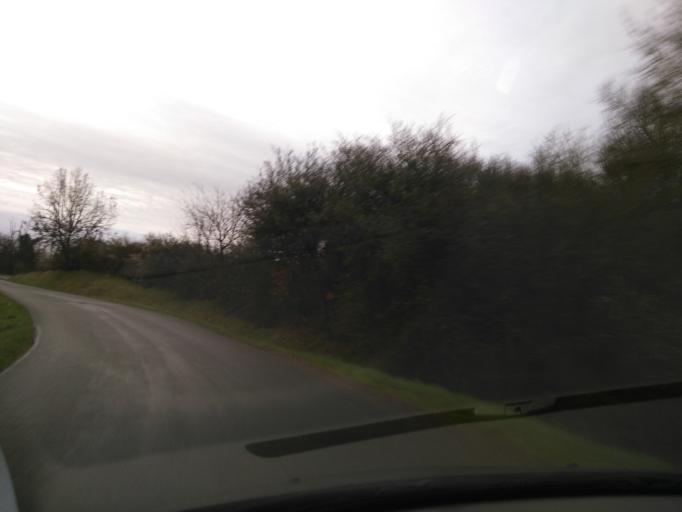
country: FR
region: Midi-Pyrenees
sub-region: Departement du Tarn-et-Garonne
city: Finhan
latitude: 43.8785
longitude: 1.1461
